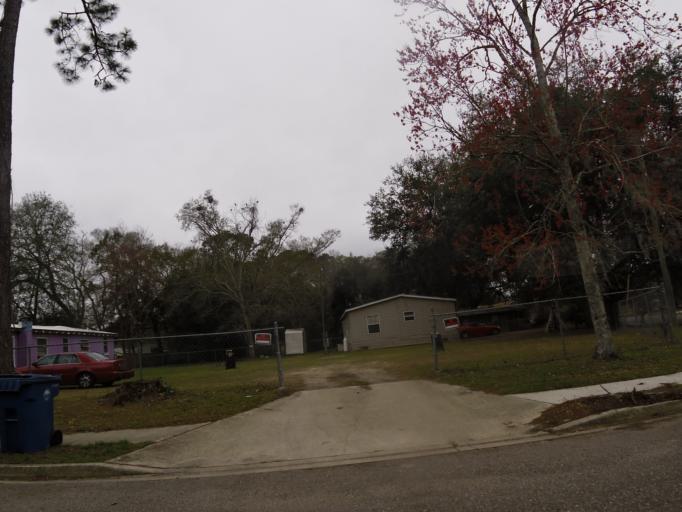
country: US
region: Florida
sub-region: Duval County
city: Jacksonville
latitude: 30.3772
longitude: -81.6959
